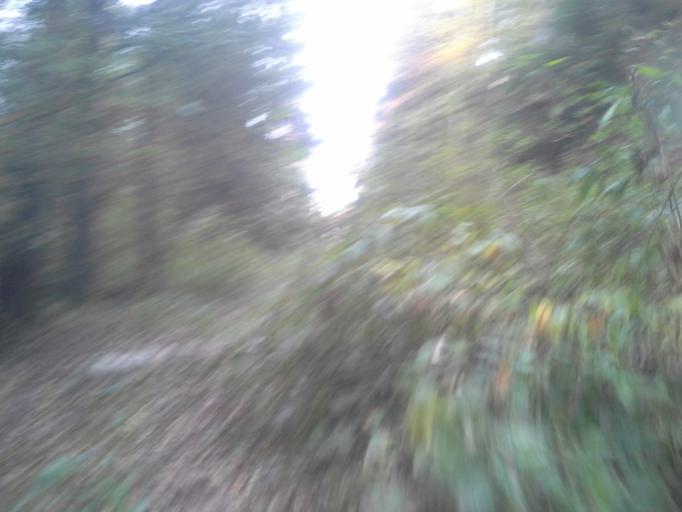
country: RU
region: Moskovskaya
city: Selyatino
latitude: 55.4561
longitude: 36.9739
